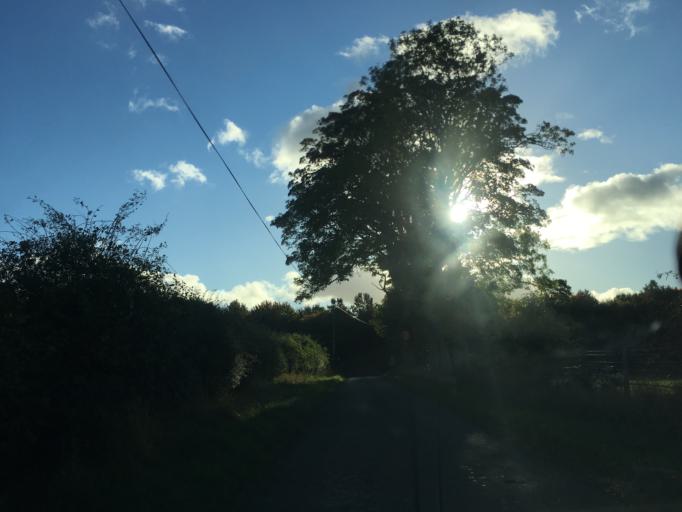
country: GB
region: Scotland
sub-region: East Lothian
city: Pencaitland
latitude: 55.8490
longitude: -2.9153
